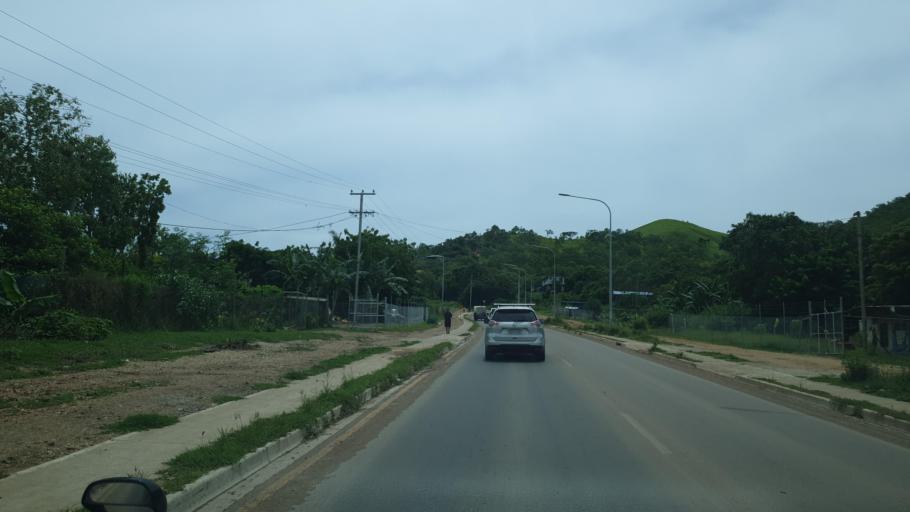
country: PG
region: National Capital
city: Port Moresby
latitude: -9.5147
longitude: 147.2407
